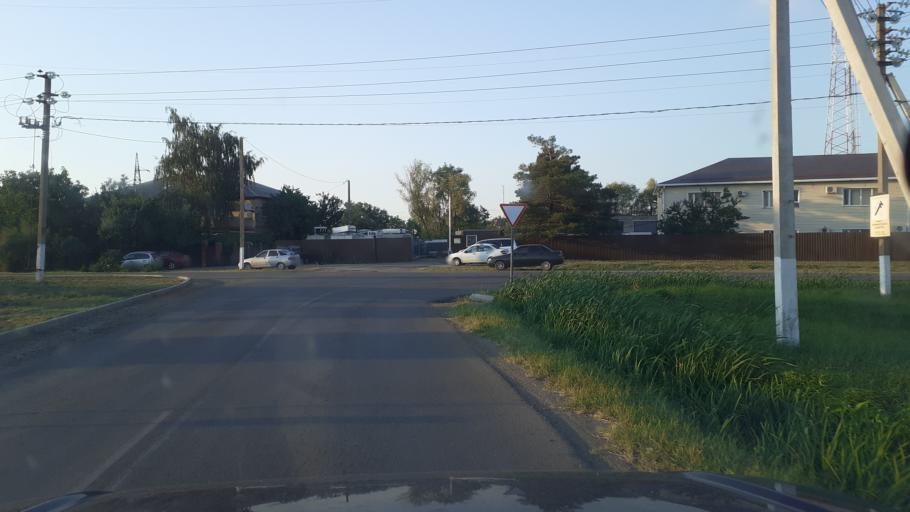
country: RU
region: Krasnodarskiy
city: Severskaya
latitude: 44.8686
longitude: 38.6632
